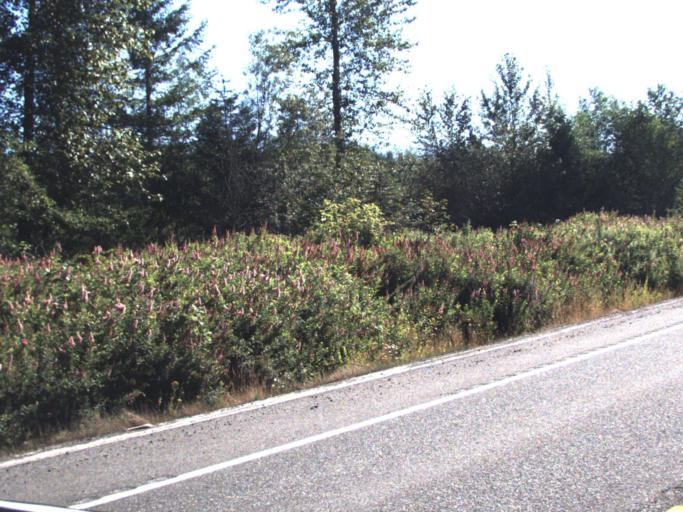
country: US
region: Washington
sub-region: King County
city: Enumclaw
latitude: 47.1633
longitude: -121.8926
